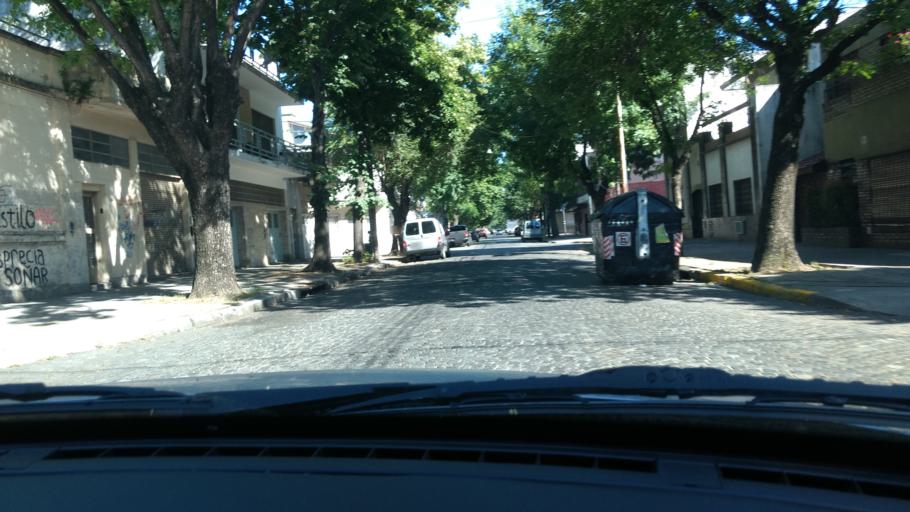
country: AR
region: Buenos Aires F.D.
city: Villa Santa Rita
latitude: -34.6124
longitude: -58.5117
